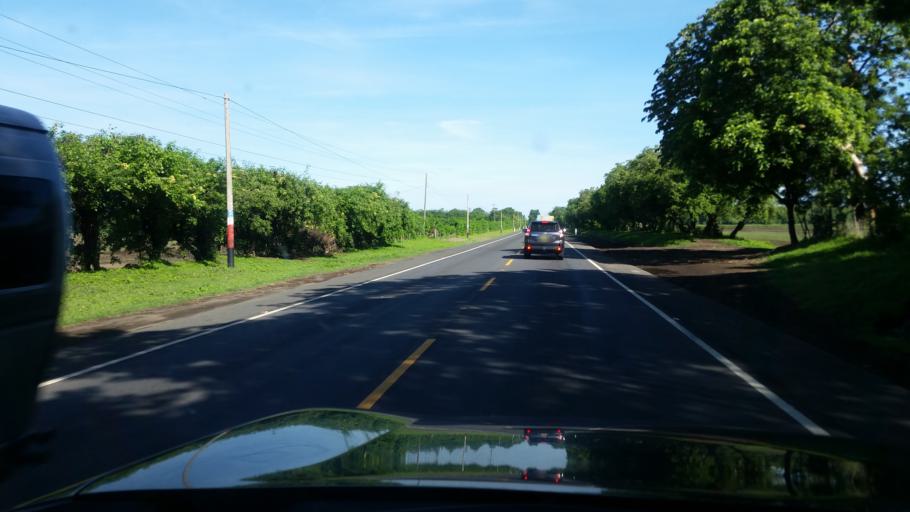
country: NI
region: Leon
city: Quezalguaque
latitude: 12.5434
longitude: -86.9188
